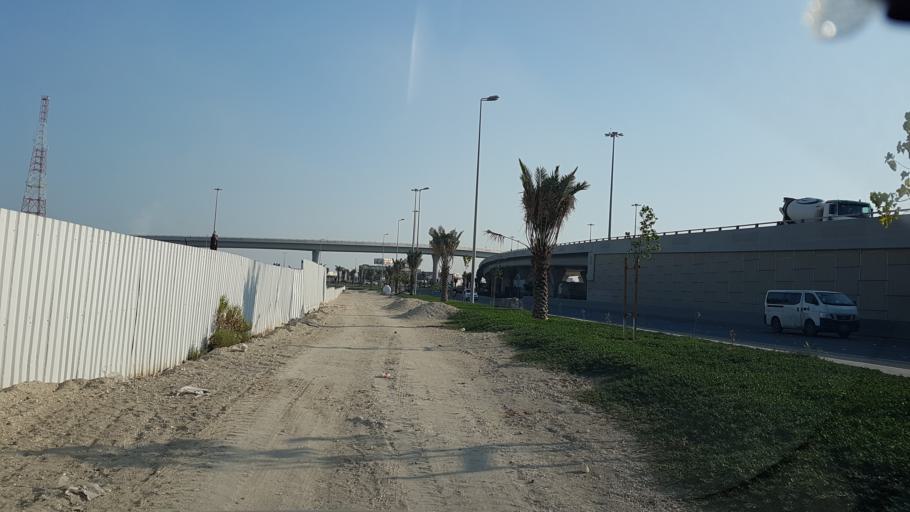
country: BH
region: Northern
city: Ar Rifa'
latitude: 26.1263
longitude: 50.5901
